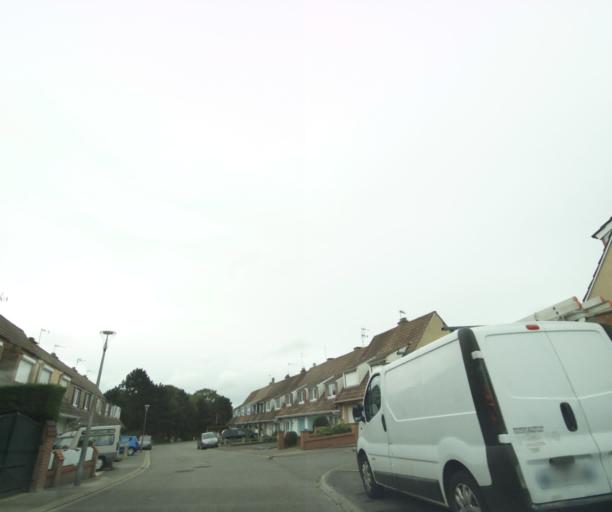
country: FR
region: Nord-Pas-de-Calais
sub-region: Departement du Pas-de-Calais
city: Etaples
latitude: 50.5228
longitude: 1.6463
